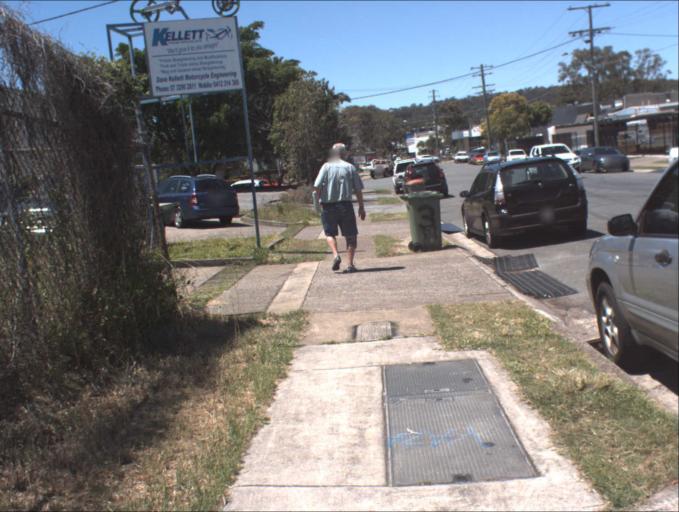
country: AU
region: Queensland
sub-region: Logan
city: Springwood
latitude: -27.6246
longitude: 153.1227
